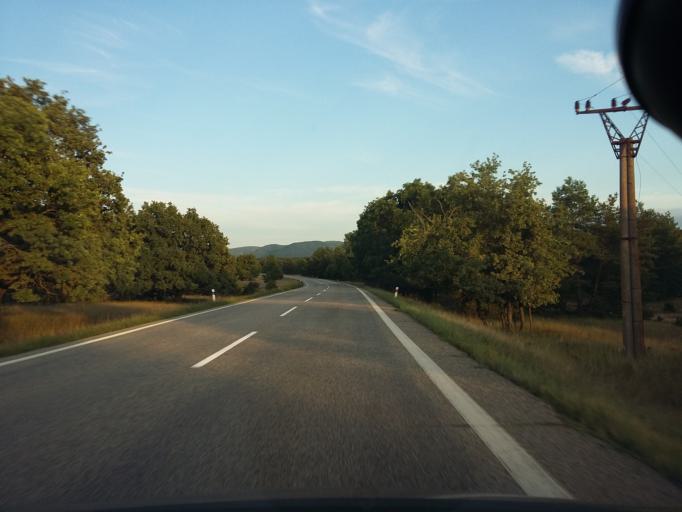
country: SK
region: Bratislavsky
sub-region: Okres Malacky
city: Malacky
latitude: 48.4111
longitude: 17.0685
